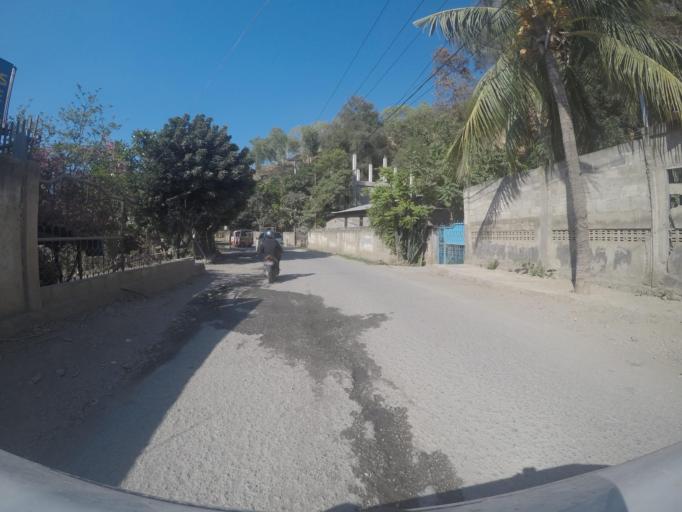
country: TL
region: Dili
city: Dili
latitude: -8.5681
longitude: 125.5479
